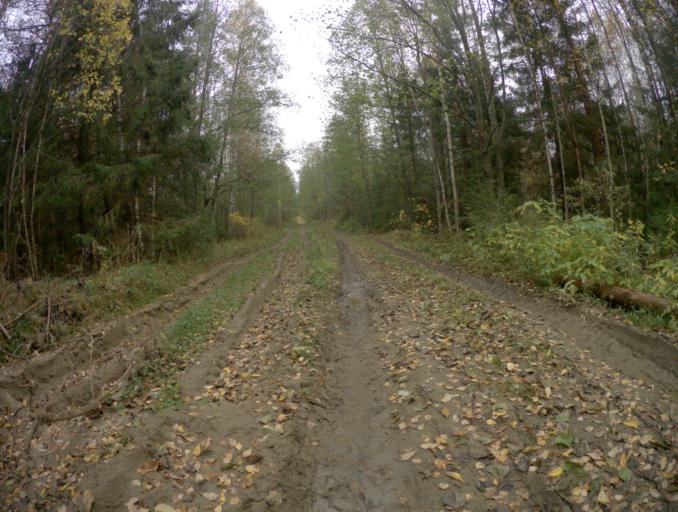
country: RU
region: Vladimir
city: Golovino
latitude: 55.9309
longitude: 40.3578
